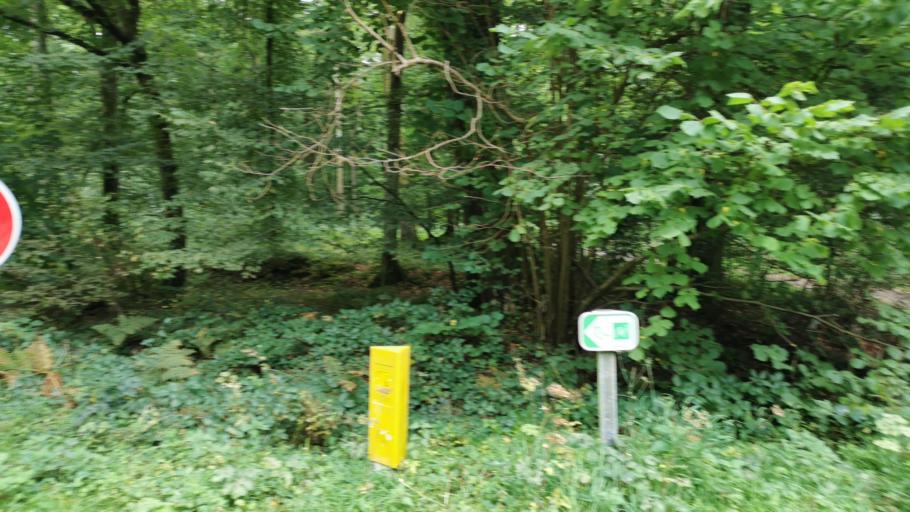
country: FR
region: Haute-Normandie
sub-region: Departement de la Seine-Maritime
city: Martin-Eglise
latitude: 49.8908
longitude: 1.1826
